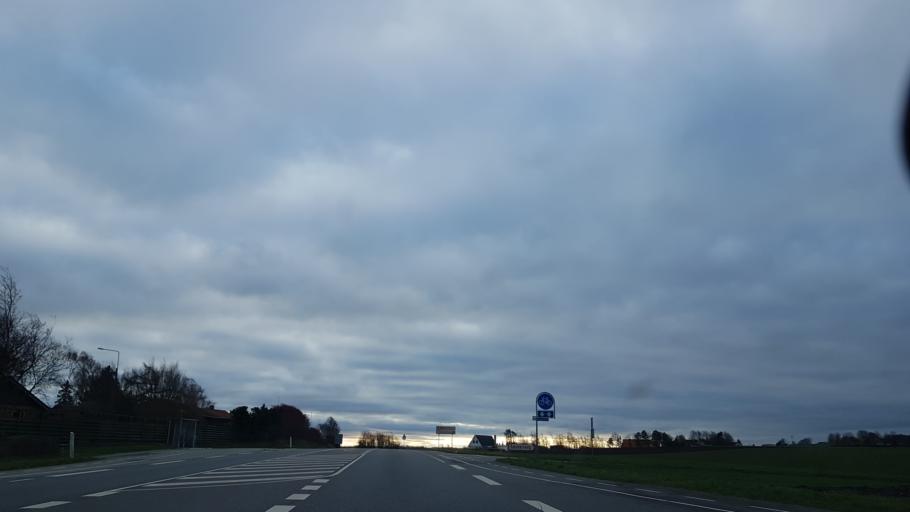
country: DK
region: Zealand
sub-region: Kalundborg Kommune
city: Gorlev
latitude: 55.5889
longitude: 11.1858
